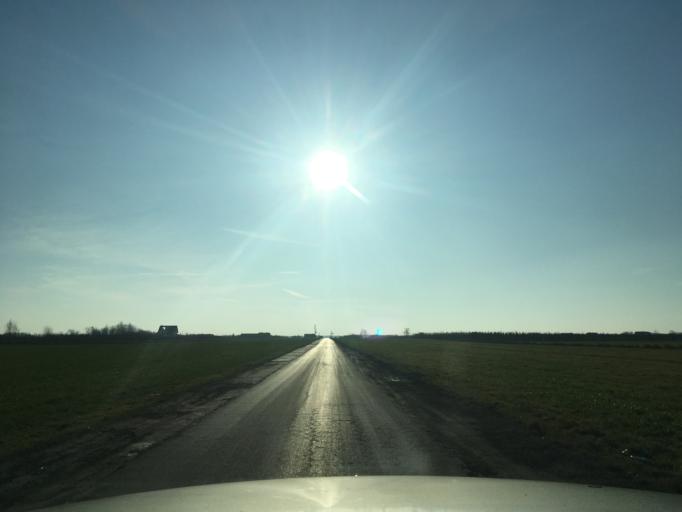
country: PL
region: Masovian Voivodeship
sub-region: Powiat pruszkowski
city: Nadarzyn
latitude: 52.0419
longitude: 20.8273
